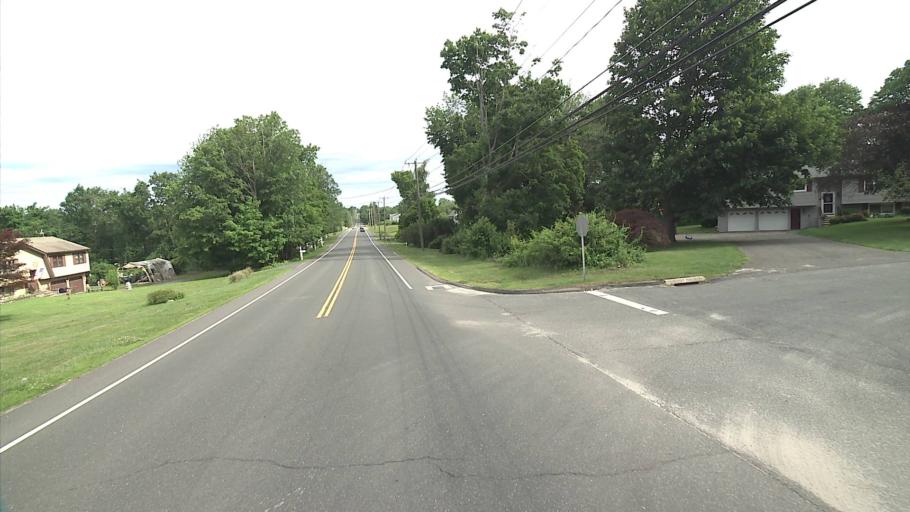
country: US
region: Connecticut
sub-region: Litchfield County
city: Watertown
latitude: 41.6294
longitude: -73.1373
